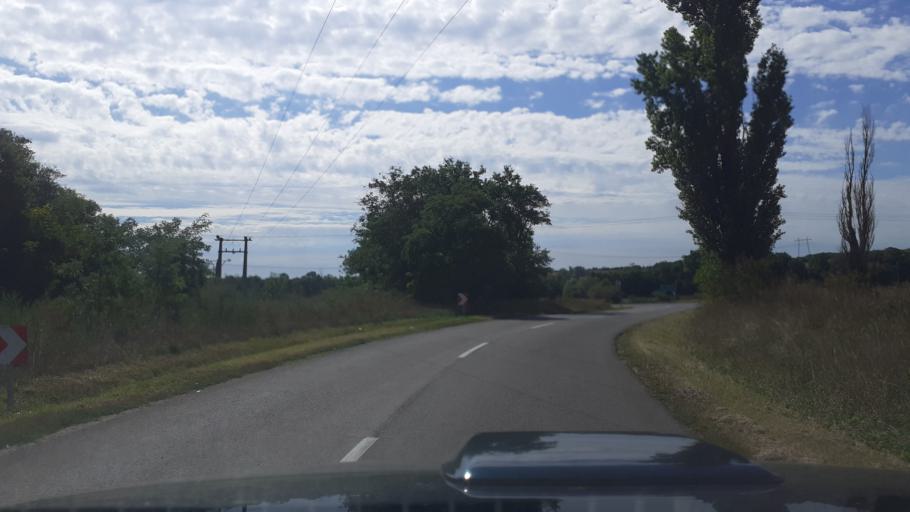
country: HU
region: Fejer
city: Pusztaszabolcs
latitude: 47.1181
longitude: 18.7805
